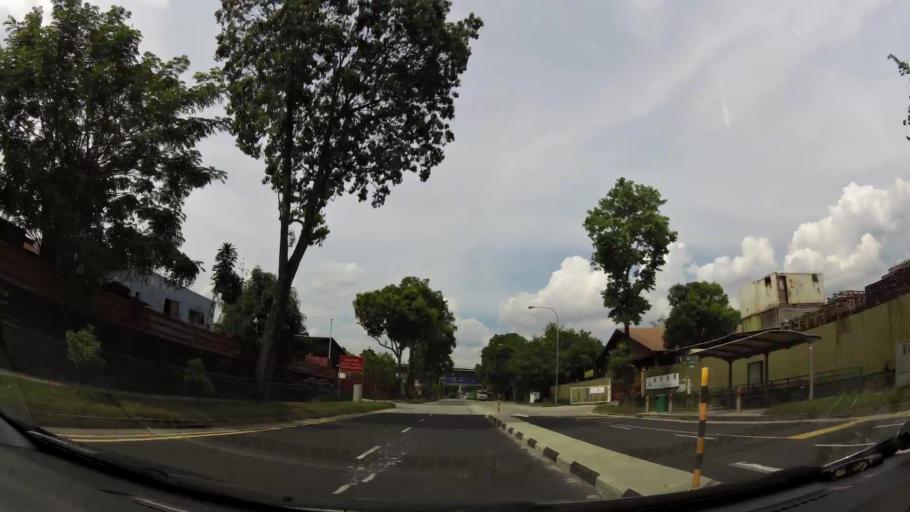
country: MY
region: Johor
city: Johor Bahru
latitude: 1.4199
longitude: 103.7507
